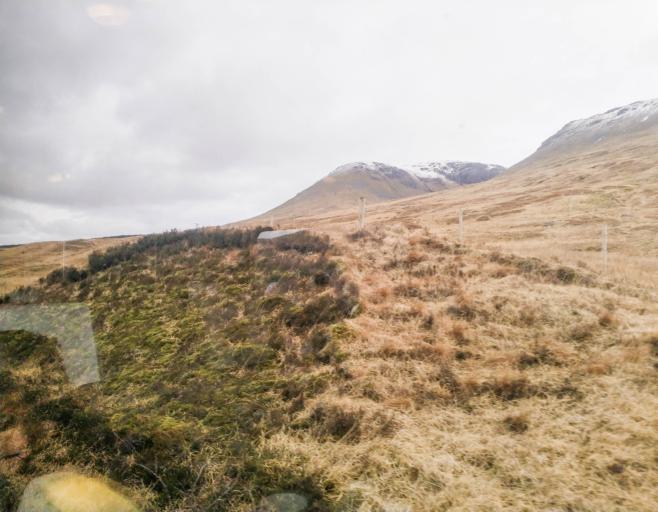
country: GB
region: Scotland
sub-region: Highland
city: Spean Bridge
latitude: 56.5083
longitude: -4.7595
